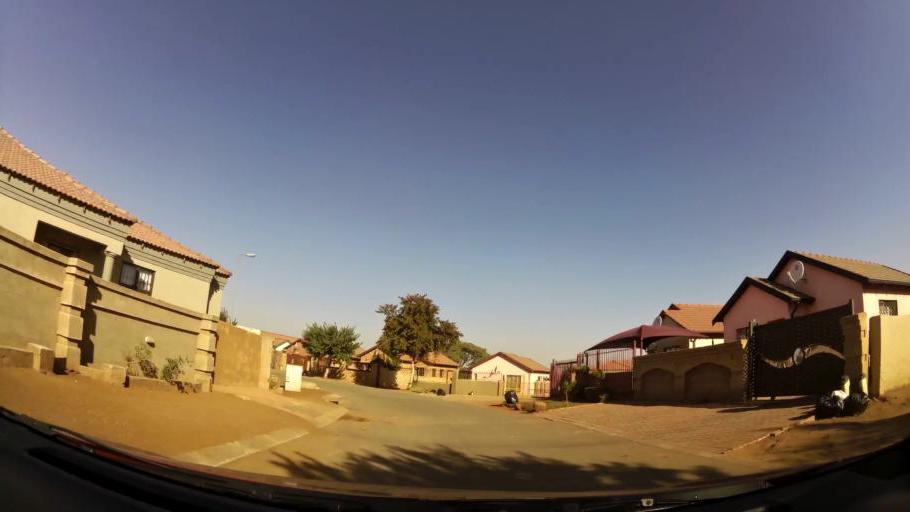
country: ZA
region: Gauteng
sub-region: City of Tshwane Metropolitan Municipality
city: Mabopane
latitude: -25.5769
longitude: 28.0898
